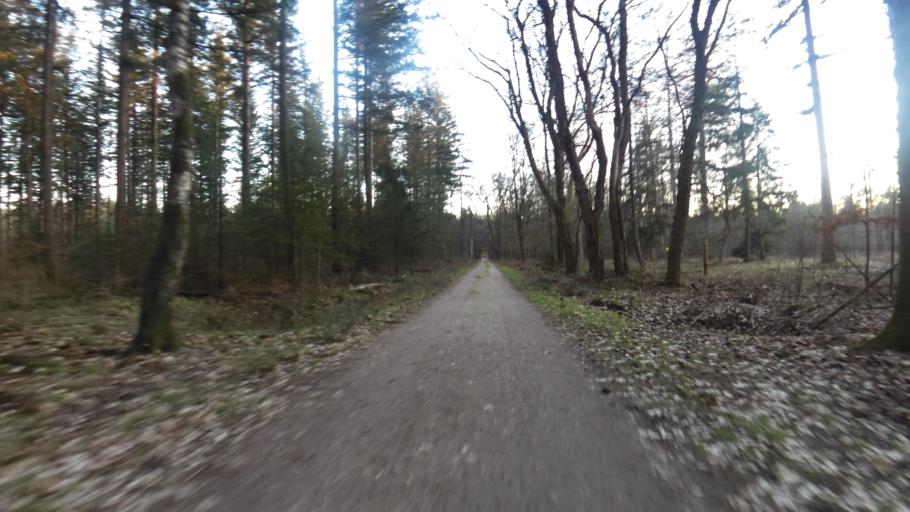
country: NL
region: Gelderland
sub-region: Gemeente Barneveld
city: Garderen
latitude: 52.2327
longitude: 5.6824
